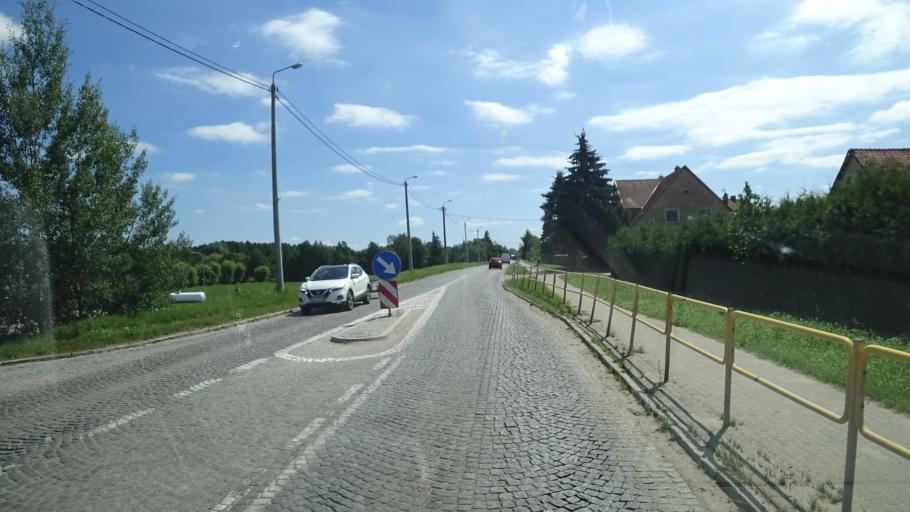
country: PL
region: Warmian-Masurian Voivodeship
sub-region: Powiat elcki
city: Prostki
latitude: 53.6937
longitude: 22.4415
